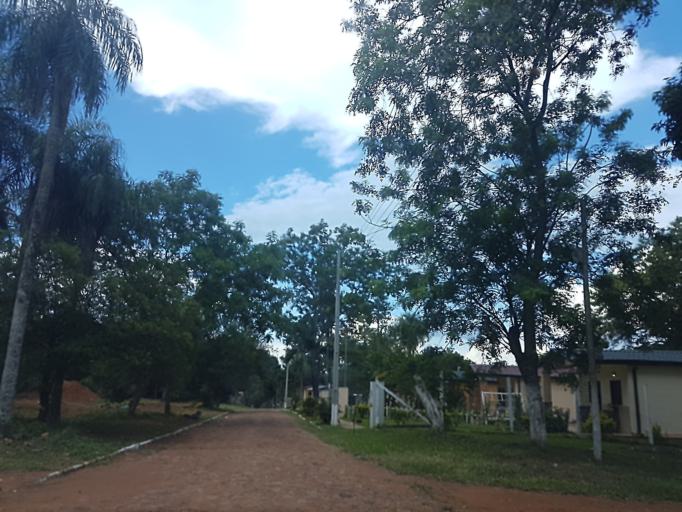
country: PY
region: Central
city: Limpio
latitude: -25.2388
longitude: -57.4455
